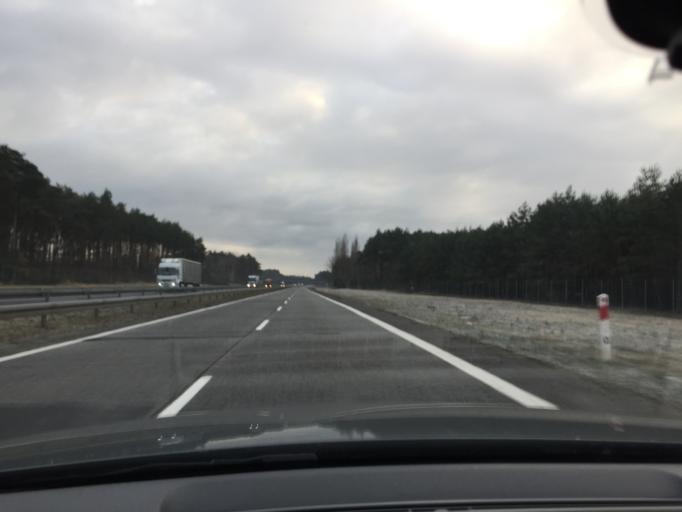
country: PL
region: Lubusz
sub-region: Powiat zarski
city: Trzebiel
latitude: 51.6453
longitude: 14.8387
